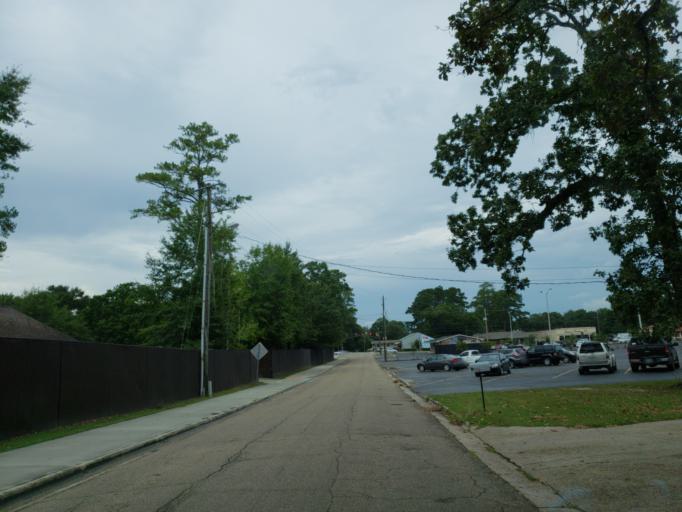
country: US
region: Mississippi
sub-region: Forrest County
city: Hattiesburg
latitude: 31.3230
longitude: -89.3143
